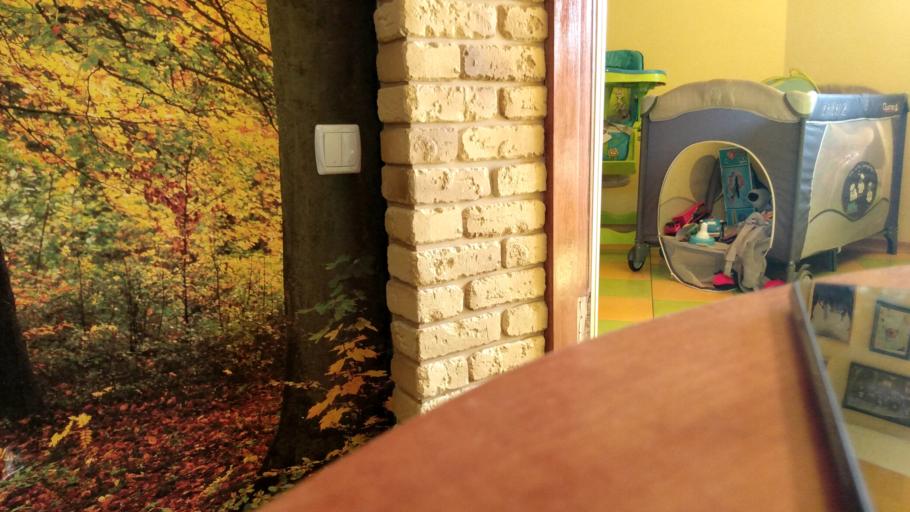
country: RU
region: Tverskaya
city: Sakharovo
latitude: 56.9286
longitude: 36.0081
